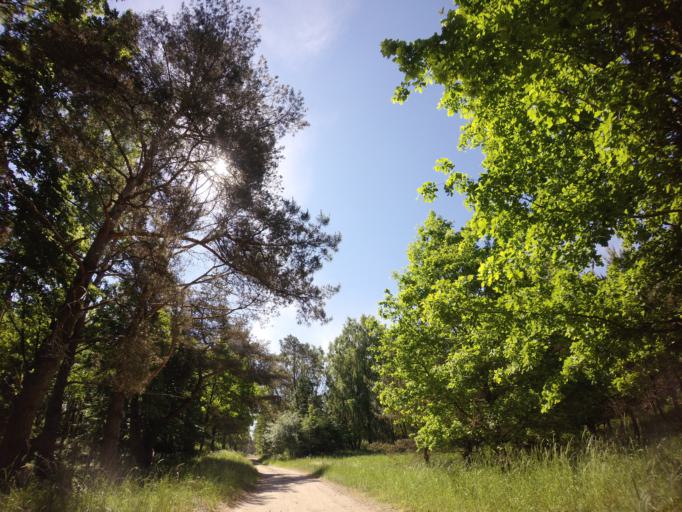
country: PL
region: West Pomeranian Voivodeship
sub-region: Powiat choszczenski
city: Recz
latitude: 53.3021
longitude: 15.6304
